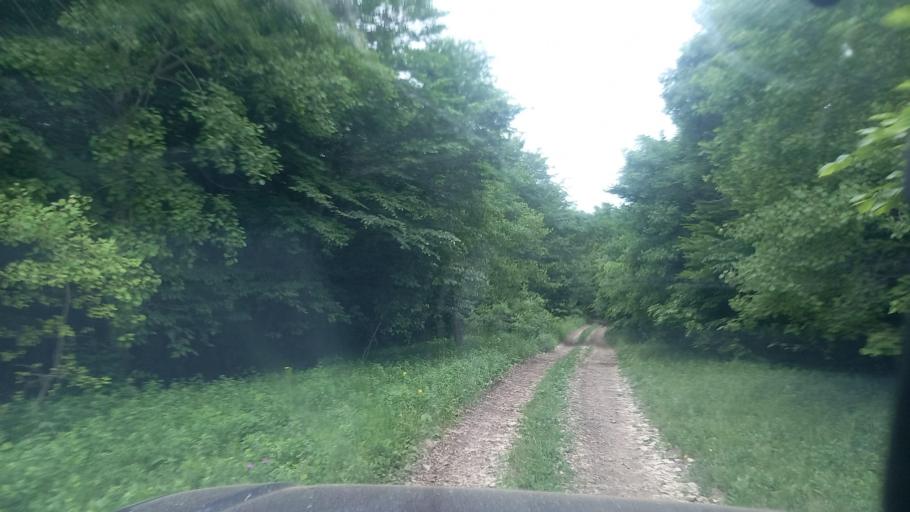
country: RU
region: Karachayevo-Cherkesiya
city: Pregradnaya
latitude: 44.0272
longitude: 41.3012
